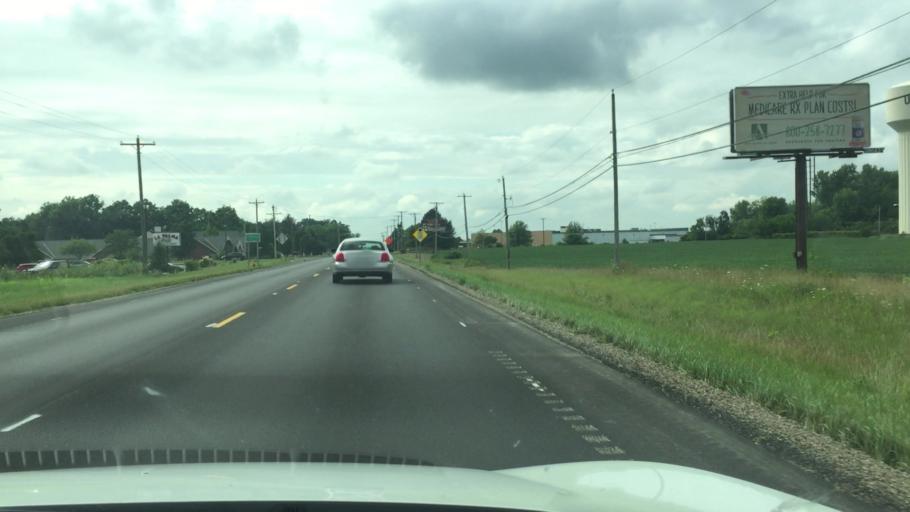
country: US
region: Ohio
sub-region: Champaign County
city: Urbana
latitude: 40.1007
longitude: -83.7164
